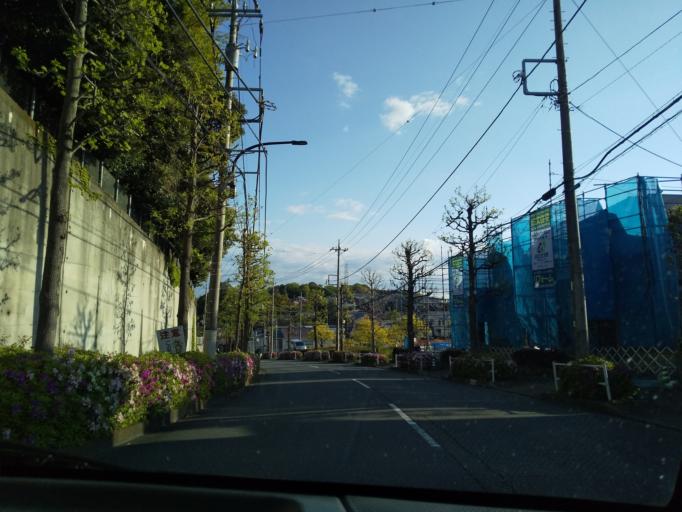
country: JP
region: Tokyo
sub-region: Machida-shi
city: Machida
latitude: 35.5746
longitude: 139.4552
